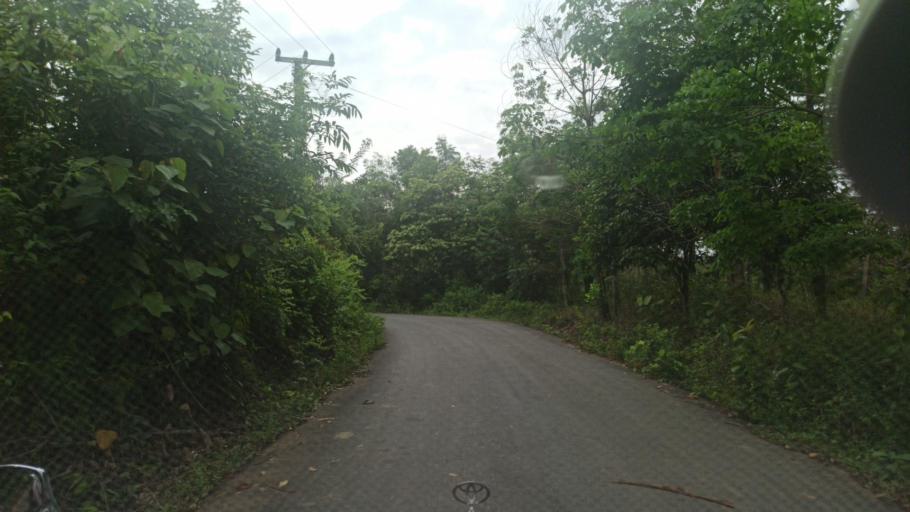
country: ID
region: South Sumatra
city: Gunungmegang Dalam
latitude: -3.3043
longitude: 103.6449
